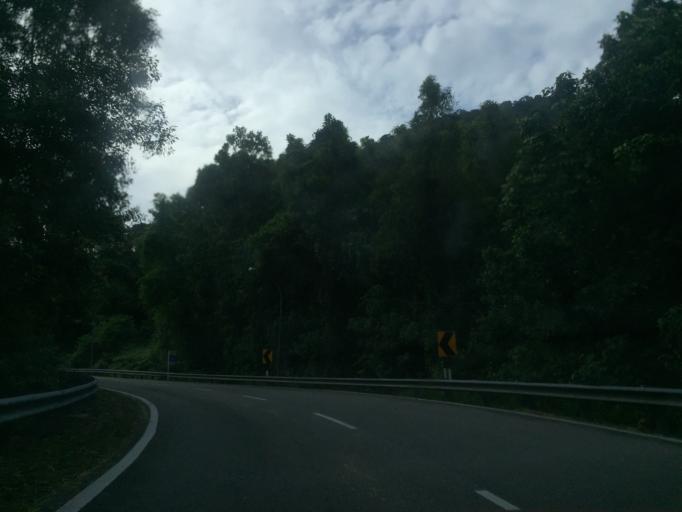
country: MY
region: Perak
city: Lumut
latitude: 4.2458
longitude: 100.5576
